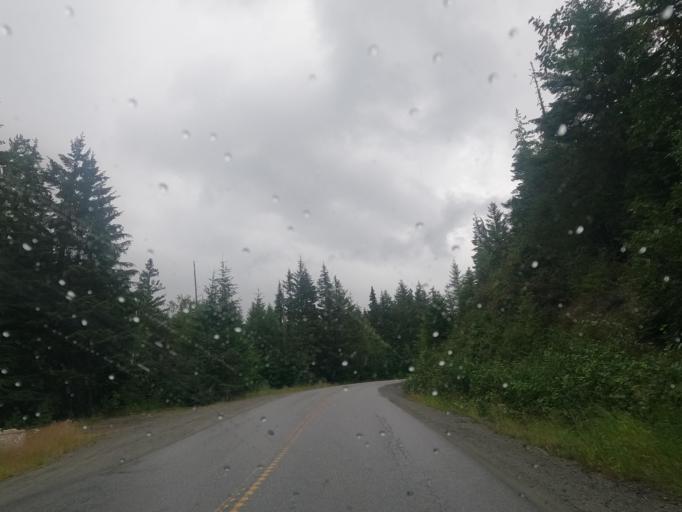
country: CA
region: British Columbia
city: Pemberton
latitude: 50.3338
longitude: -122.5493
